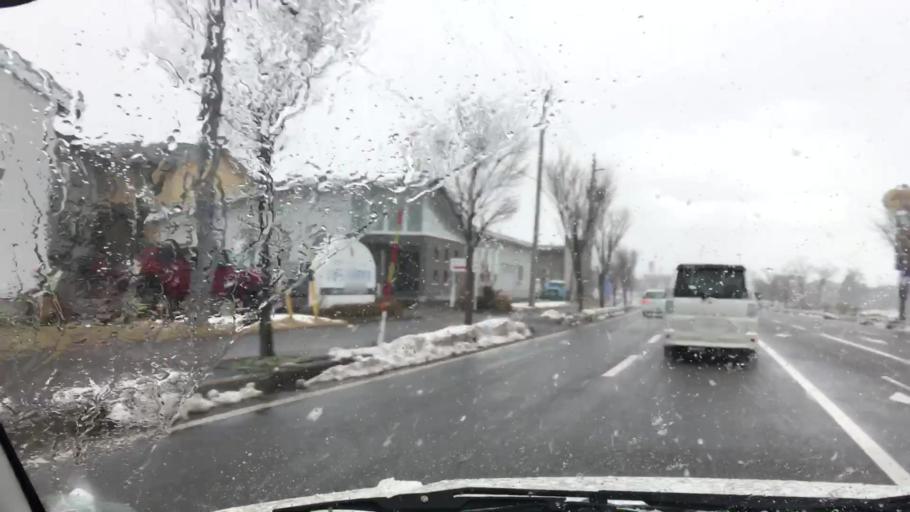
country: JP
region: Niigata
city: Joetsu
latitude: 37.1146
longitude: 138.2330
